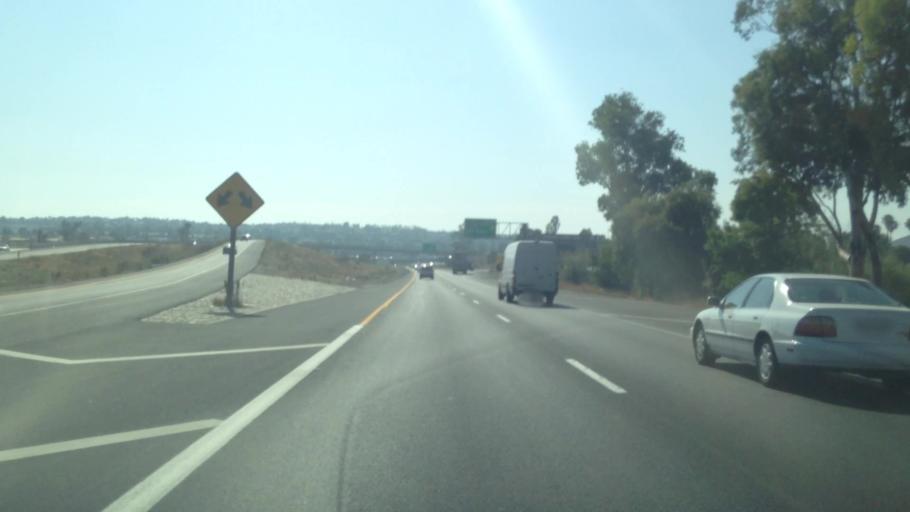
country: US
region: California
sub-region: Riverside County
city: Moreno Valley
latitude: 33.9444
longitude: -117.2879
